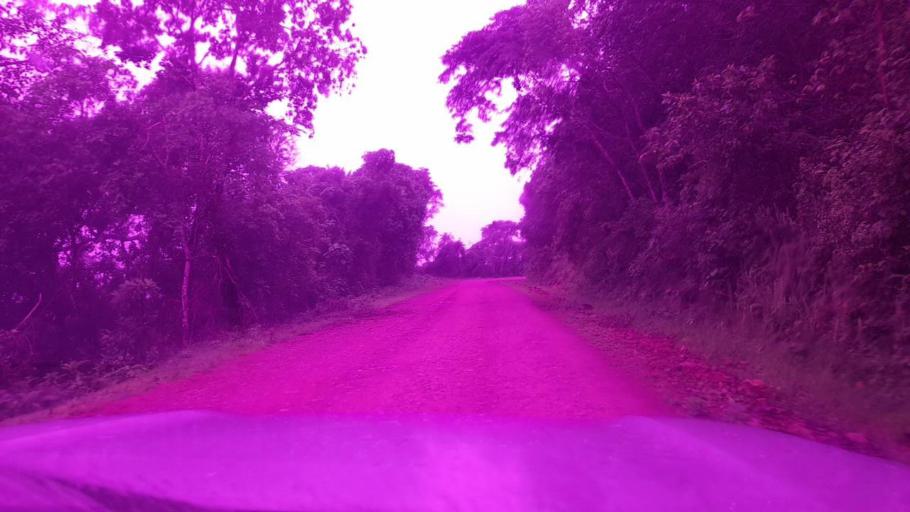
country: ET
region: Southern Nations, Nationalities, and People's Region
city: Bonga
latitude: 7.5205
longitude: 36.0573
